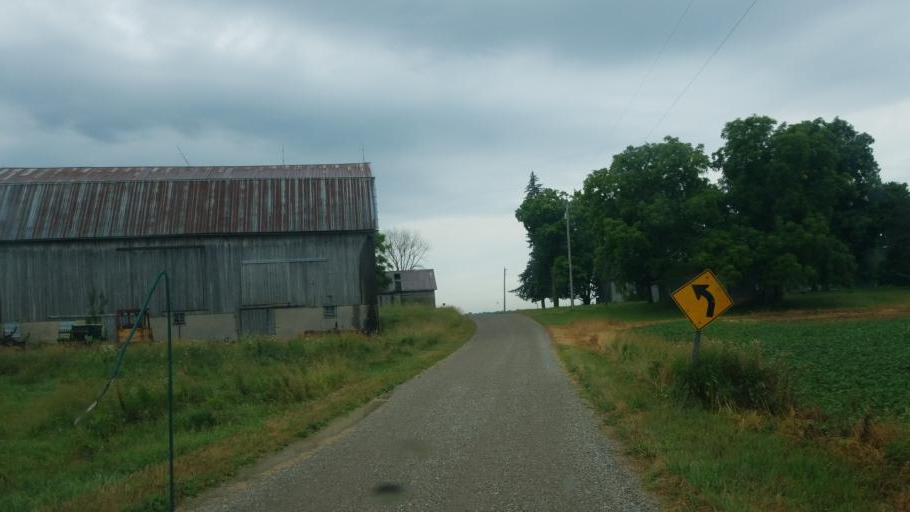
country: US
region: Indiana
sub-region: Steuben County
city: Hamilton
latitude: 41.5011
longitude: -84.9413
